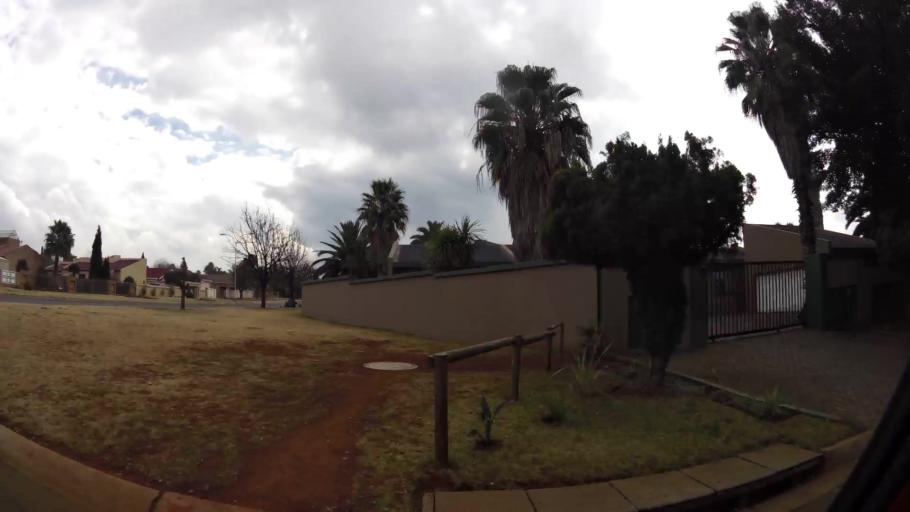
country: ZA
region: Gauteng
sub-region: Sedibeng District Municipality
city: Vanderbijlpark
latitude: -26.7348
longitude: 27.8547
